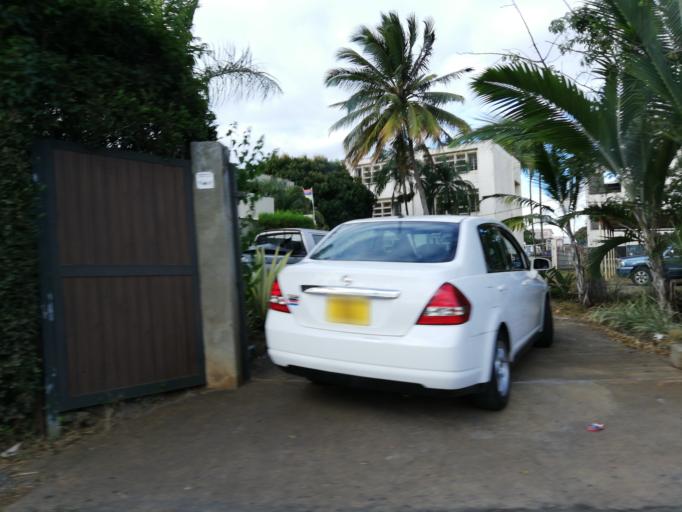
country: MU
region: Black River
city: Petite Riviere
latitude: -20.2201
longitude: 57.4608
